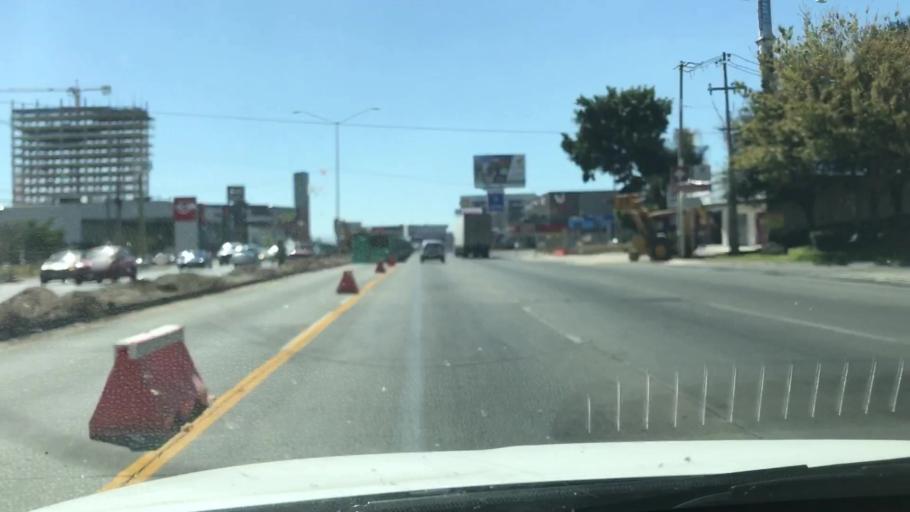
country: MX
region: Jalisco
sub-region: Tlajomulco de Zuniga
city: La Tijera
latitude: 20.5732
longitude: -103.4549
